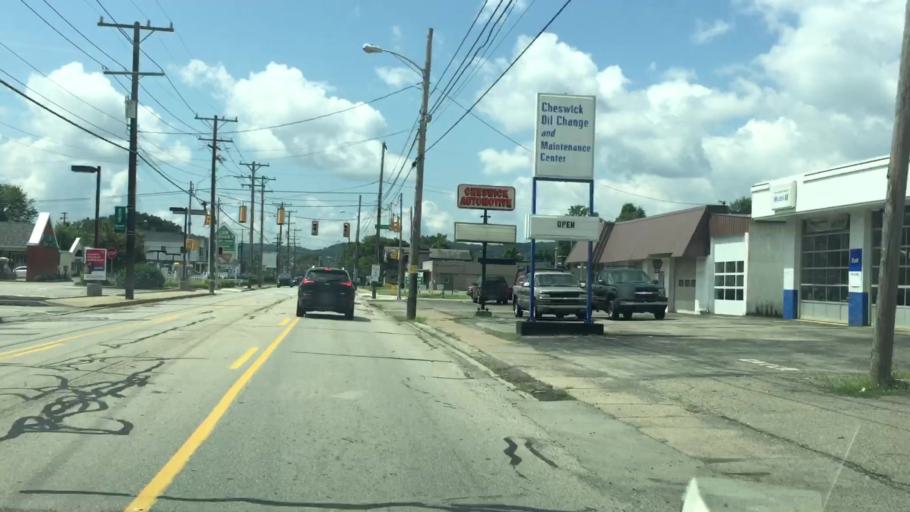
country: US
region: Pennsylvania
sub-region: Allegheny County
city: Cheswick
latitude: 40.5411
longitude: -79.8032
